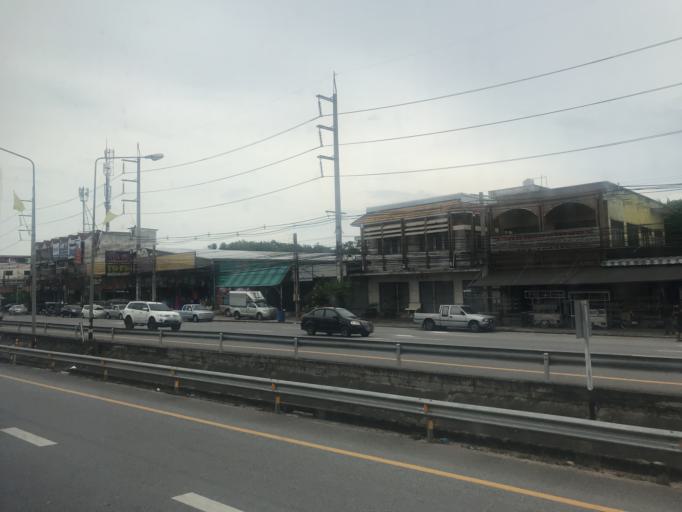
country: TH
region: Chon Buri
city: Bang Lamung
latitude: 13.0190
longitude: 100.9320
